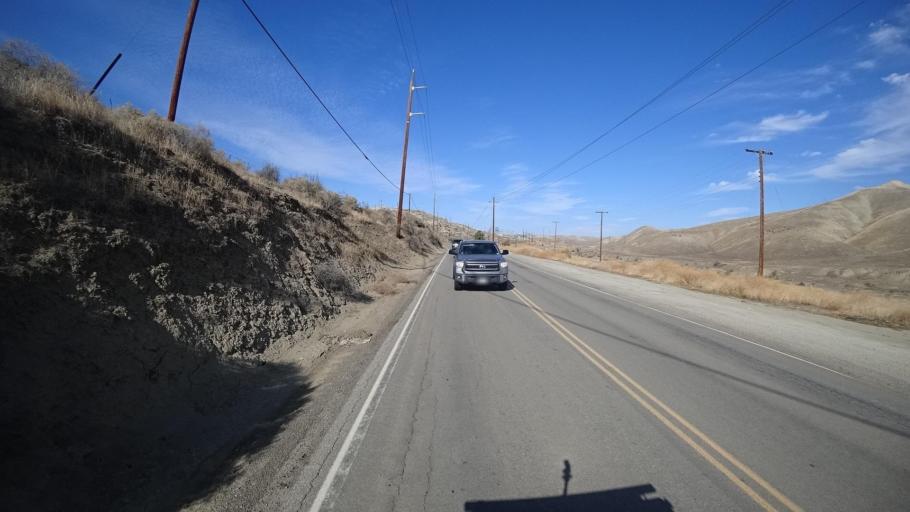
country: US
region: California
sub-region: Kern County
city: Oildale
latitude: 35.5539
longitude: -118.9586
